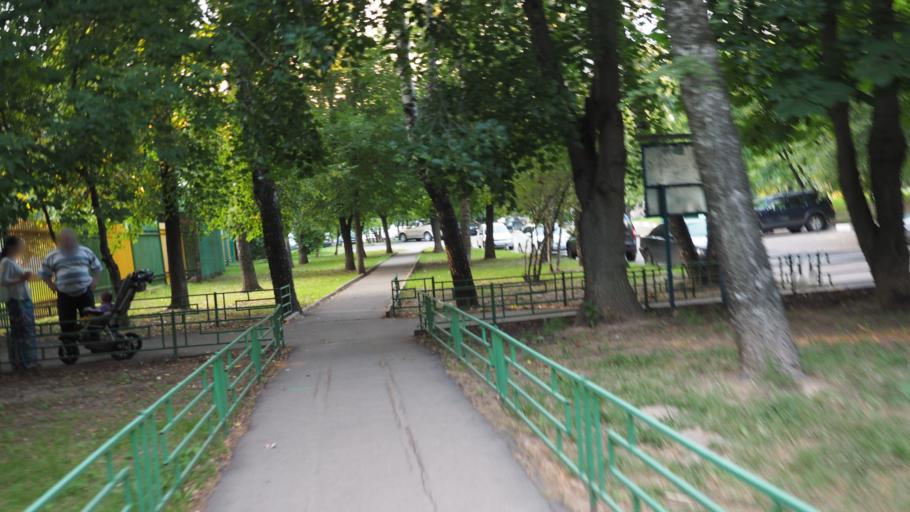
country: RU
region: Moscow
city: Orekhovo-Borisovo
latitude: 55.6020
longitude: 37.7121
